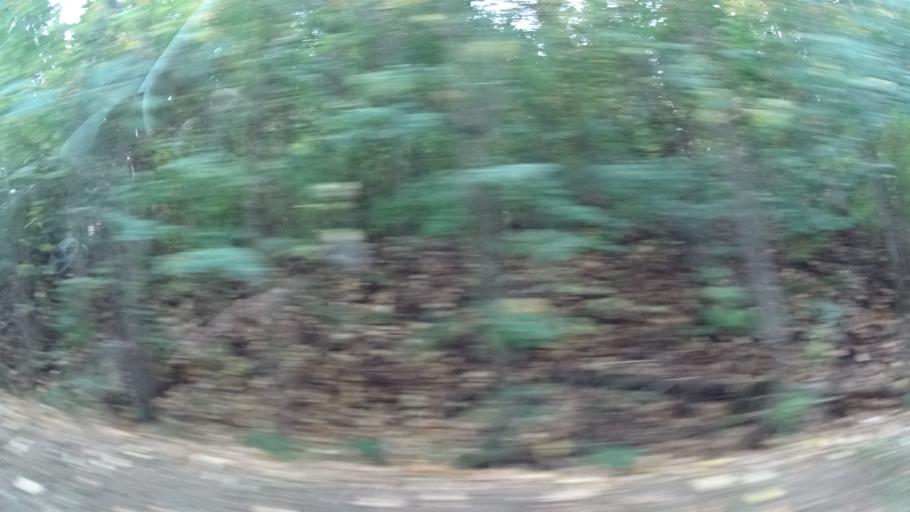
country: DE
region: Thuringia
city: Altersbach
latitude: 50.7194
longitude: 10.5290
